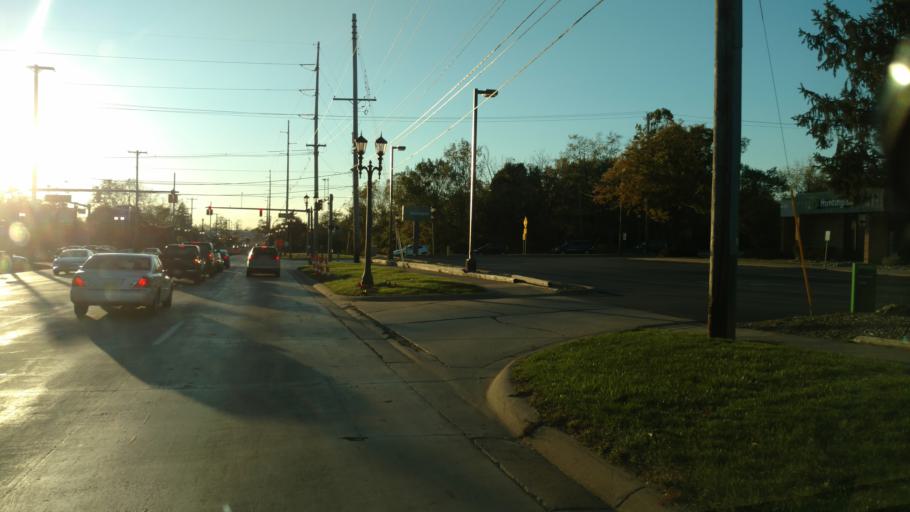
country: US
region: Michigan
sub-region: Ingham County
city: Lansing
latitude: 42.7608
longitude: -84.5222
